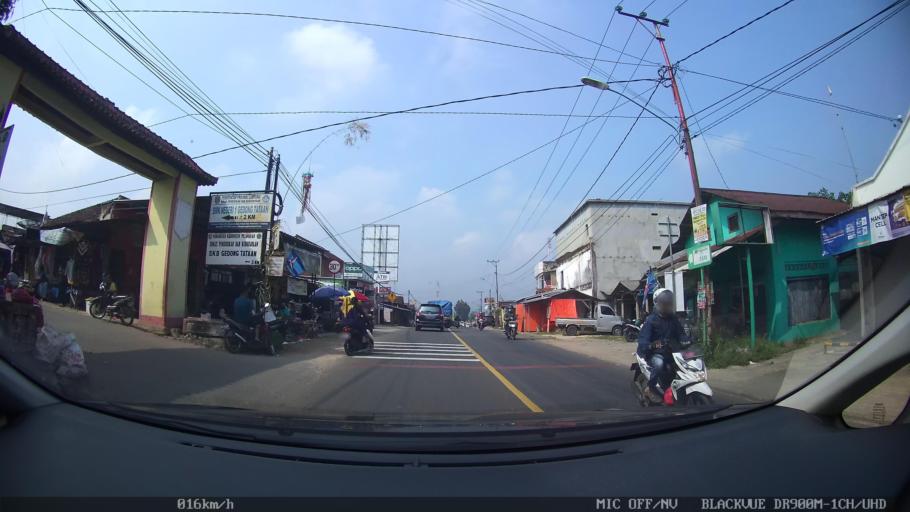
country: ID
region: Lampung
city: Gedongtataan
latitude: -5.3731
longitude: 105.1300
